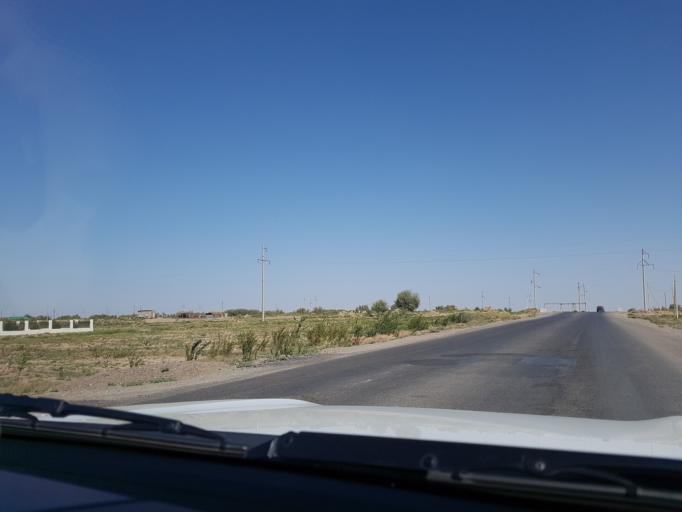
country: IR
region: Razavi Khorasan
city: Sarakhs
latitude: 36.5240
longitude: 61.2344
